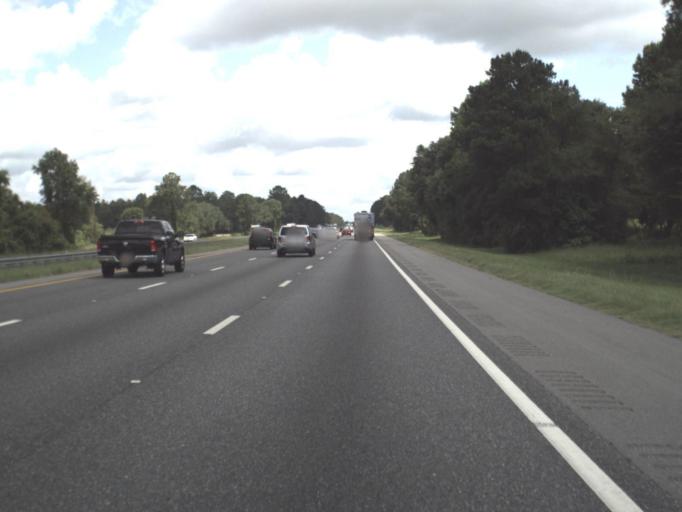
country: US
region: Florida
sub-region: Columbia County
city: Lake City
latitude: 30.0283
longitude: -82.6127
